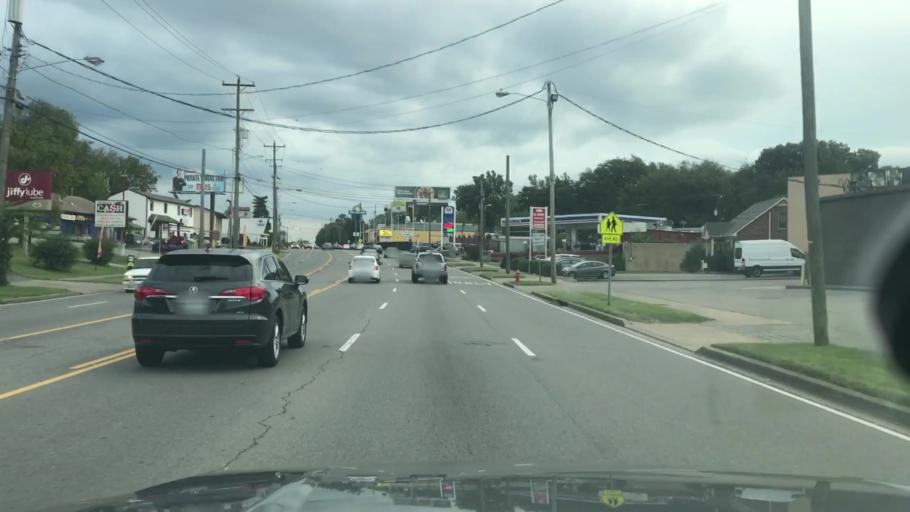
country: US
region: Tennessee
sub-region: Davidson County
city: Belle Meade
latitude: 36.1464
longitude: -86.8581
